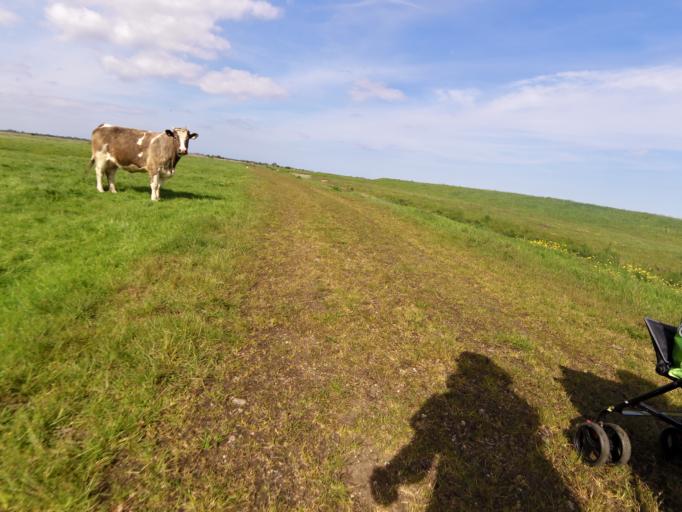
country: GB
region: England
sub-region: Norfolk
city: Great Yarmouth
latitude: 52.6125
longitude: 1.6868
